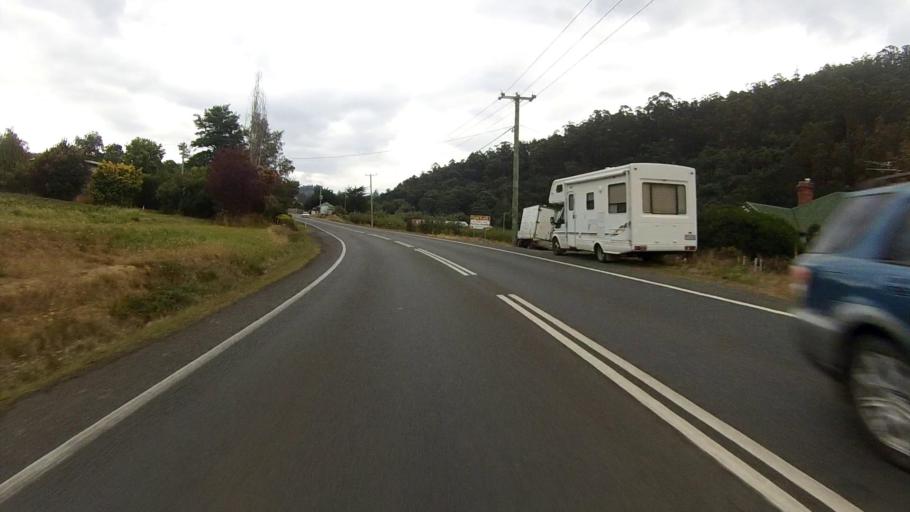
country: AU
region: Tasmania
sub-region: Huon Valley
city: Cygnet
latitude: -43.1411
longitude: 147.0633
